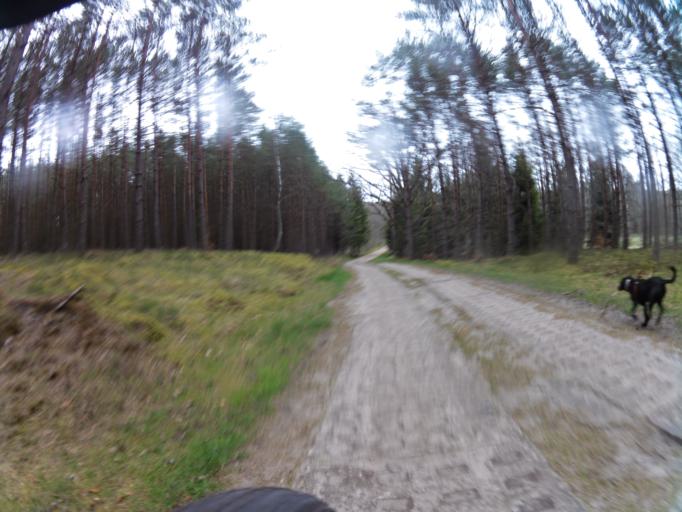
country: PL
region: West Pomeranian Voivodeship
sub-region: Powiat koszalinski
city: Bobolice
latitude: 54.0446
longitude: 16.6195
